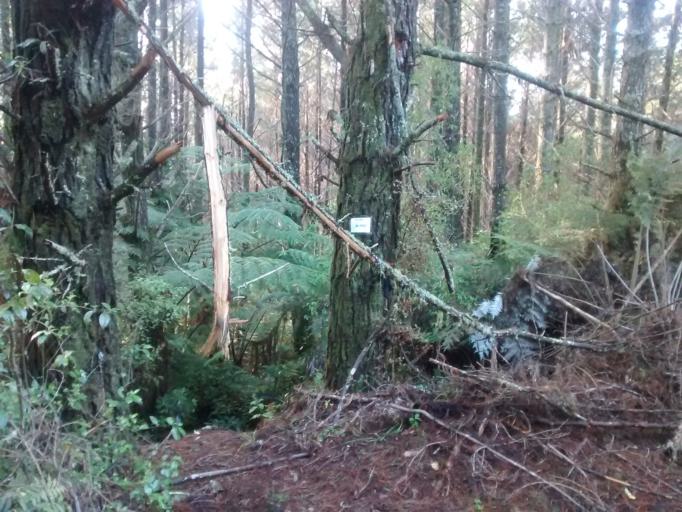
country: NZ
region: Auckland
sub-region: Auckland
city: Muriwai Beach
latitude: -36.7251
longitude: 174.5793
